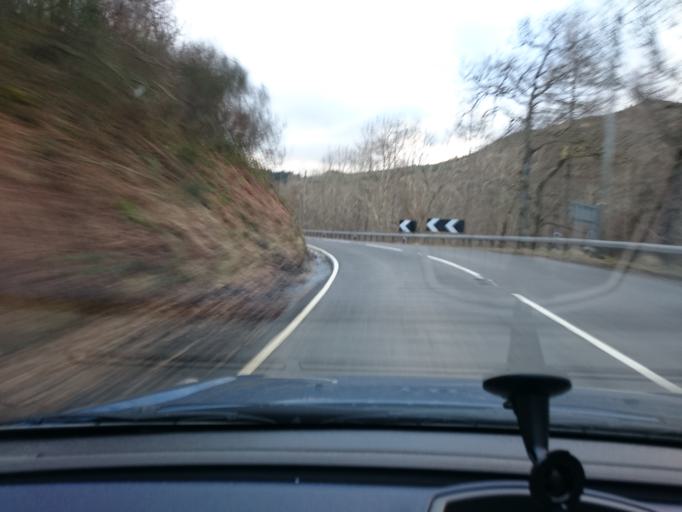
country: GB
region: Scotland
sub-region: Stirling
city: Callander
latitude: 56.2524
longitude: -4.2810
